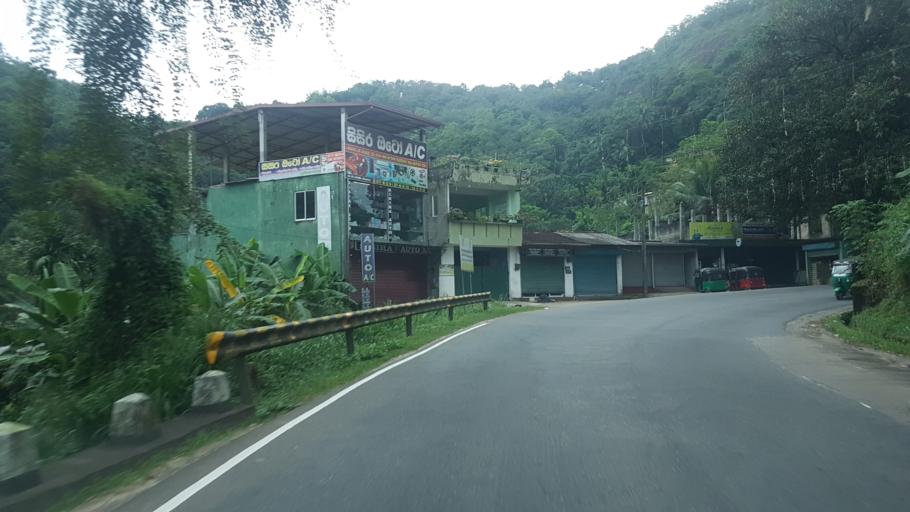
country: LK
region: Western
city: Hanwella Ihala
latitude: 7.0358
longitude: 80.2910
